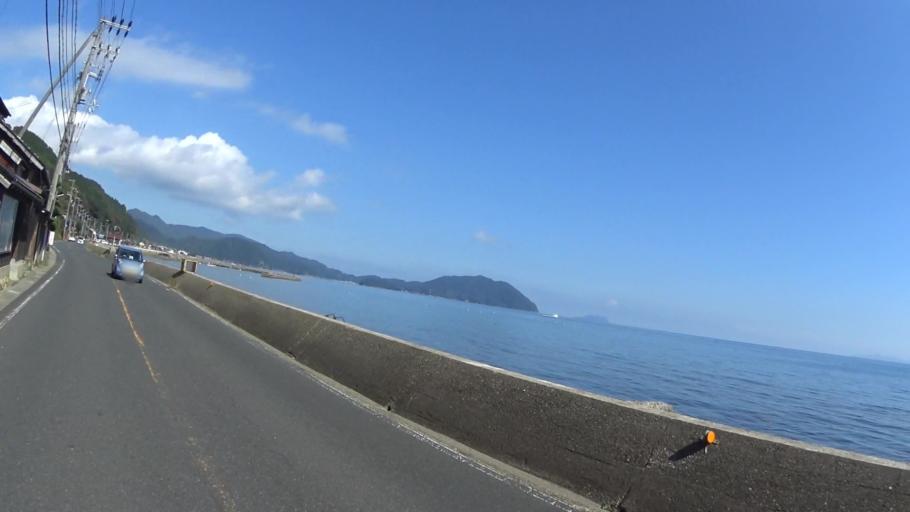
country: JP
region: Kyoto
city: Miyazu
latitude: 35.6461
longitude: 135.2513
